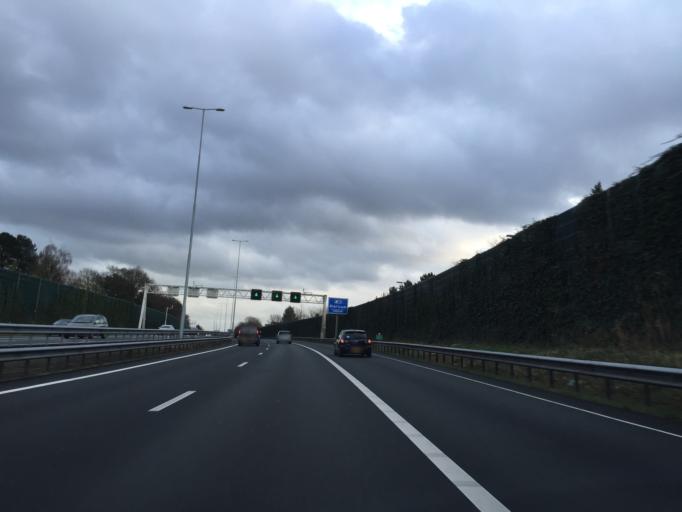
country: NL
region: North Holland
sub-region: Gemeente Bussum
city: Bussum
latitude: 52.2761
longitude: 5.1872
